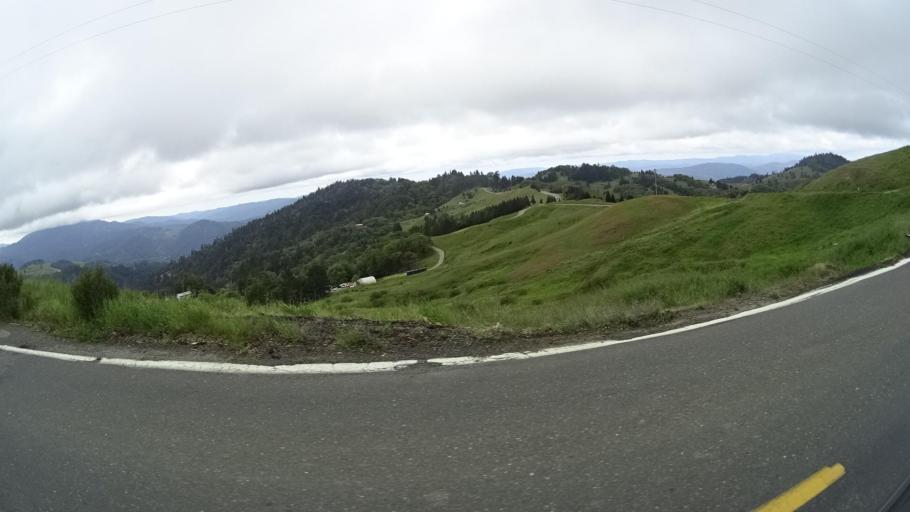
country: US
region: California
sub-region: Humboldt County
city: Redway
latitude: 40.1133
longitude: -123.7363
